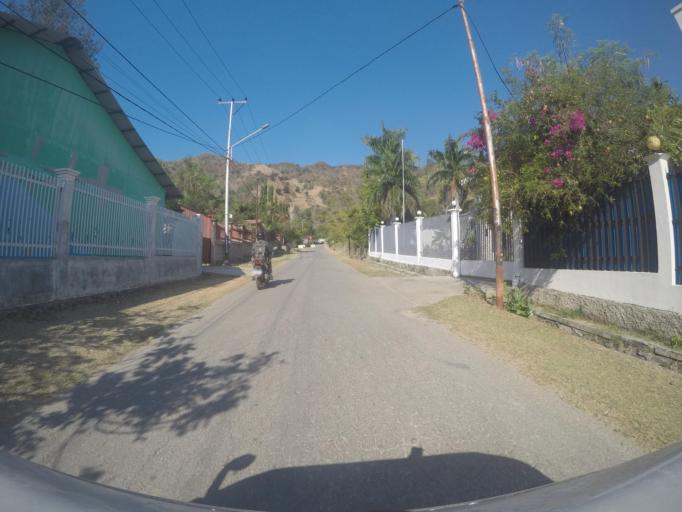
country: TL
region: Dili
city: Dili
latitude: -8.5389
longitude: 125.6152
